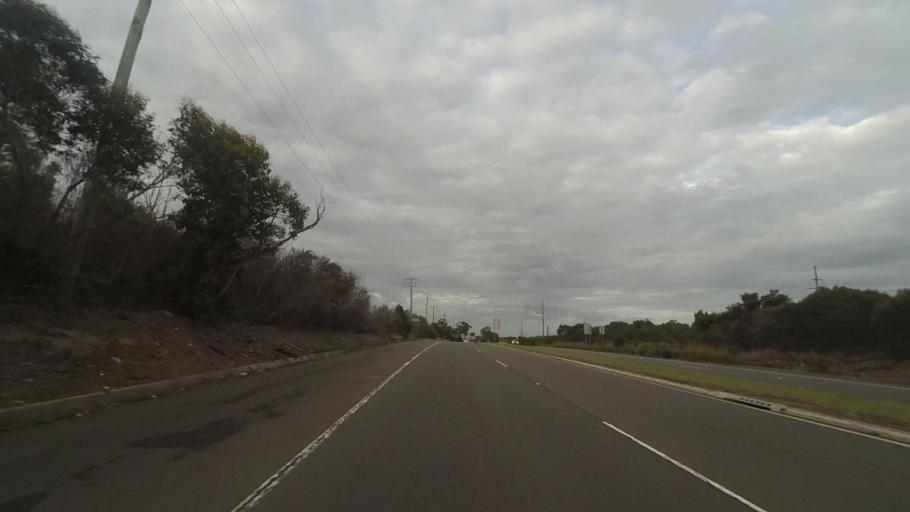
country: AU
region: New South Wales
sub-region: Sutherland Shire
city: Heathcote
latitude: -34.1000
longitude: 150.9956
